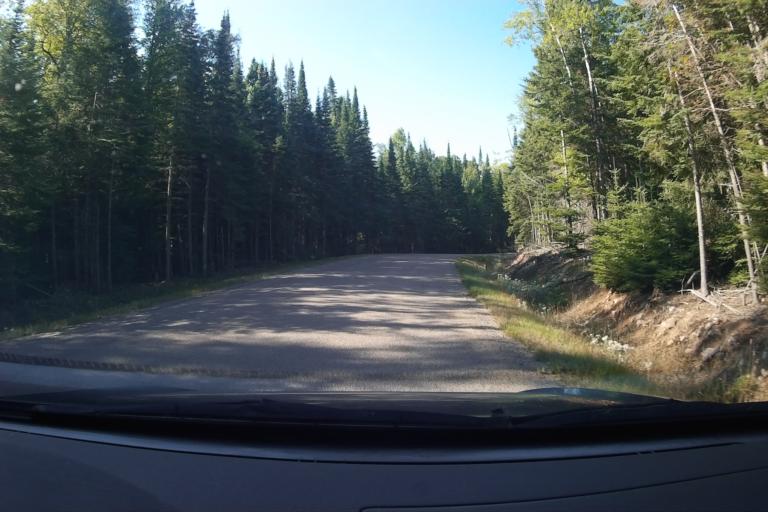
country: CA
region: Ontario
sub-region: Thunder Bay District
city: Thunder Bay
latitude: 48.3413
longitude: -88.8192
